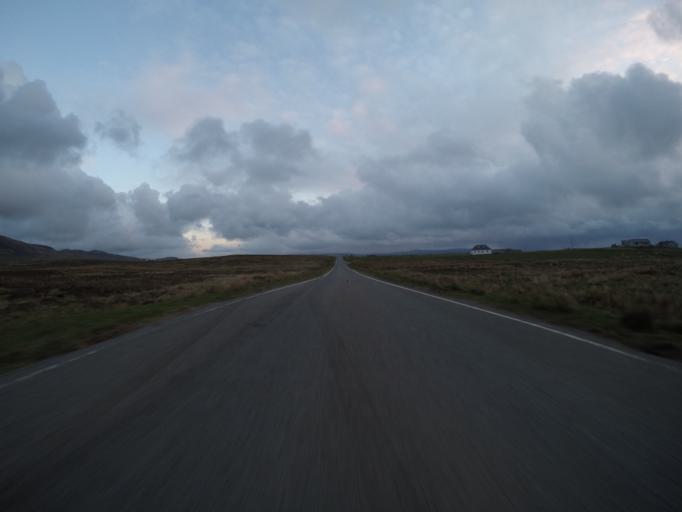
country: GB
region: Scotland
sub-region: Highland
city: Portree
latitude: 57.6564
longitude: -6.3763
